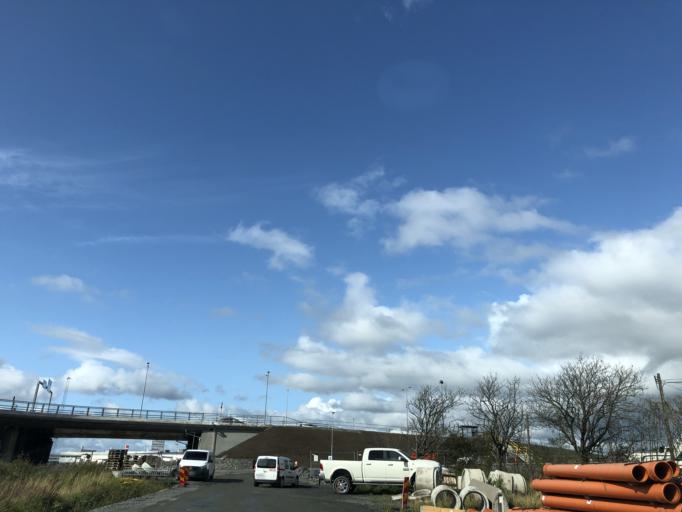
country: SE
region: Vaestra Goetaland
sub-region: Goteborg
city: Torslanda
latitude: 57.7116
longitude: 11.8431
